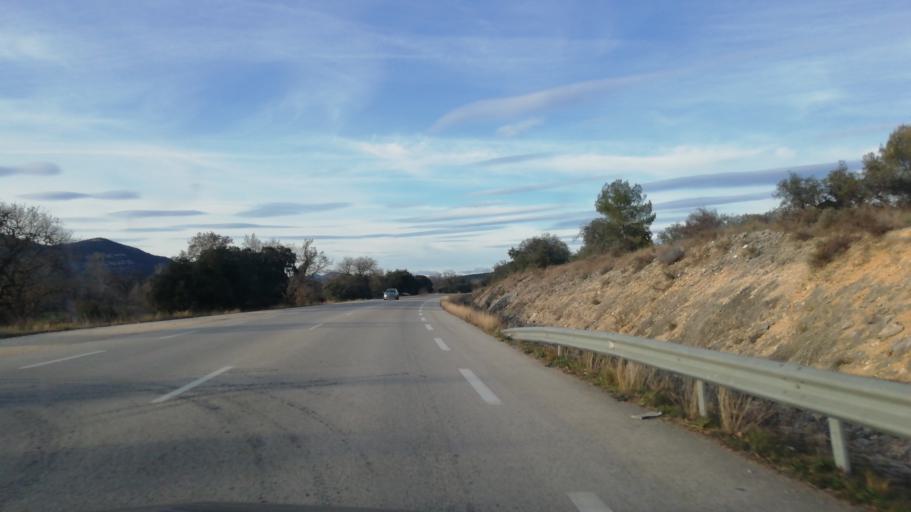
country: FR
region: Languedoc-Roussillon
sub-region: Departement du Gard
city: Quissac
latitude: 43.8957
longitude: 4.0085
